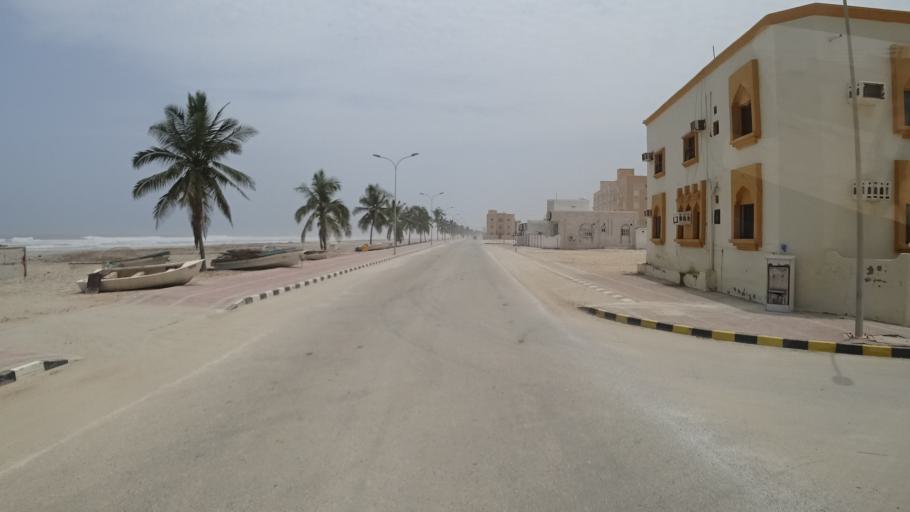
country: OM
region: Zufar
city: Salalah
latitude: 17.0345
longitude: 54.4020
